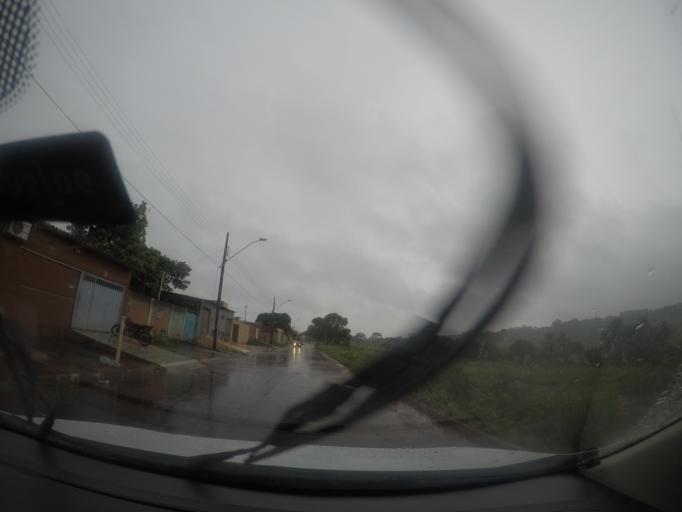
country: BR
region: Goias
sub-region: Goianira
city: Goianira
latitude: -16.5977
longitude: -49.3527
